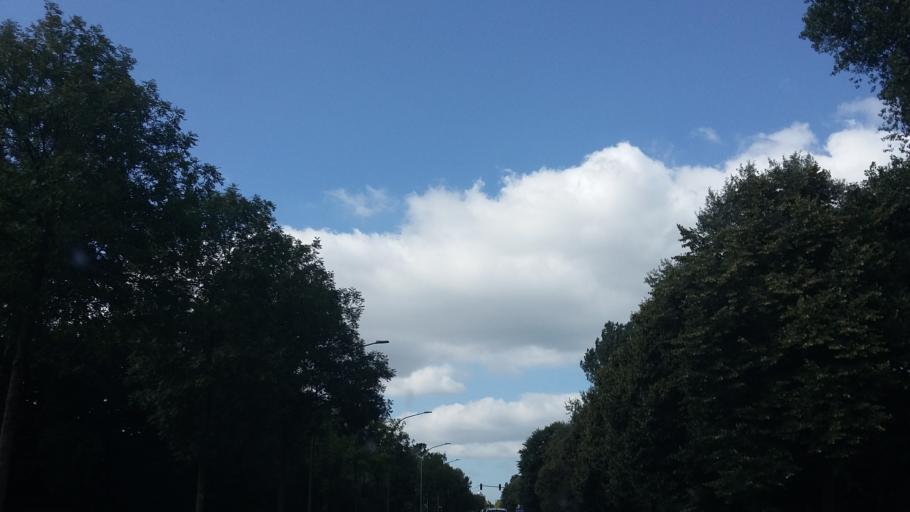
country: DE
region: Lower Saxony
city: Loxstedt
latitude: 53.4907
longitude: 8.6025
